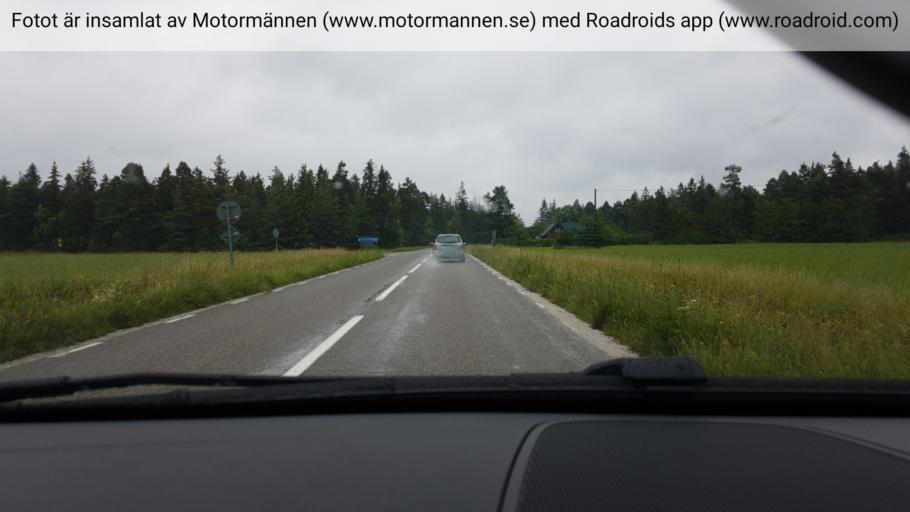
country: SE
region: Gotland
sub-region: Gotland
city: Slite
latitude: 57.5878
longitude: 18.7298
